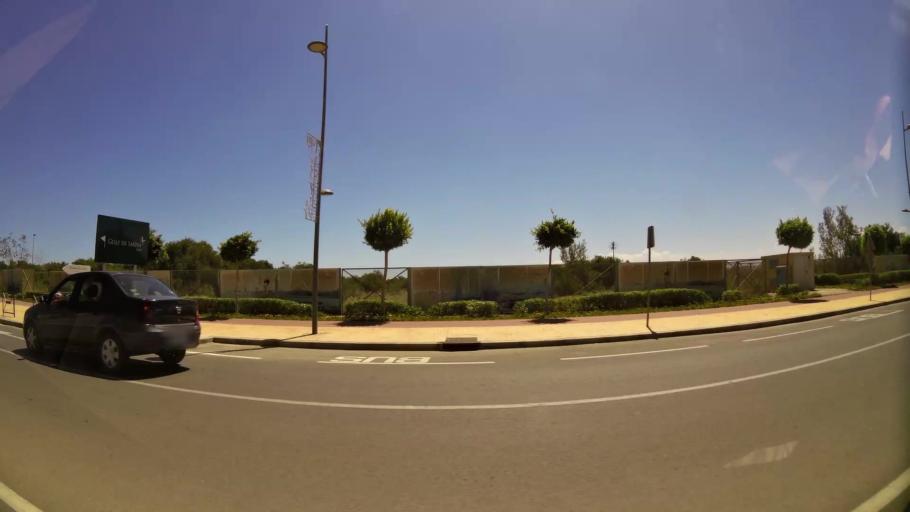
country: MA
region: Oriental
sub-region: Berkane-Taourirt
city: Madagh
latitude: 35.1047
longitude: -2.3002
